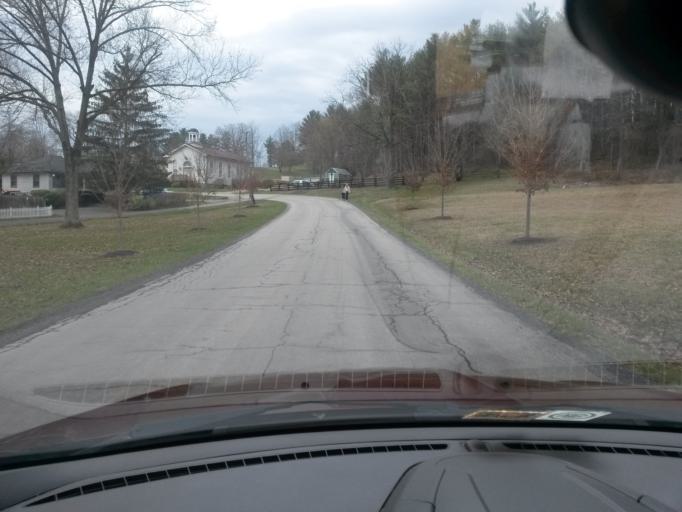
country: US
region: Virginia
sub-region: Bath County
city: Warm Springs
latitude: 38.0544
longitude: -79.8430
